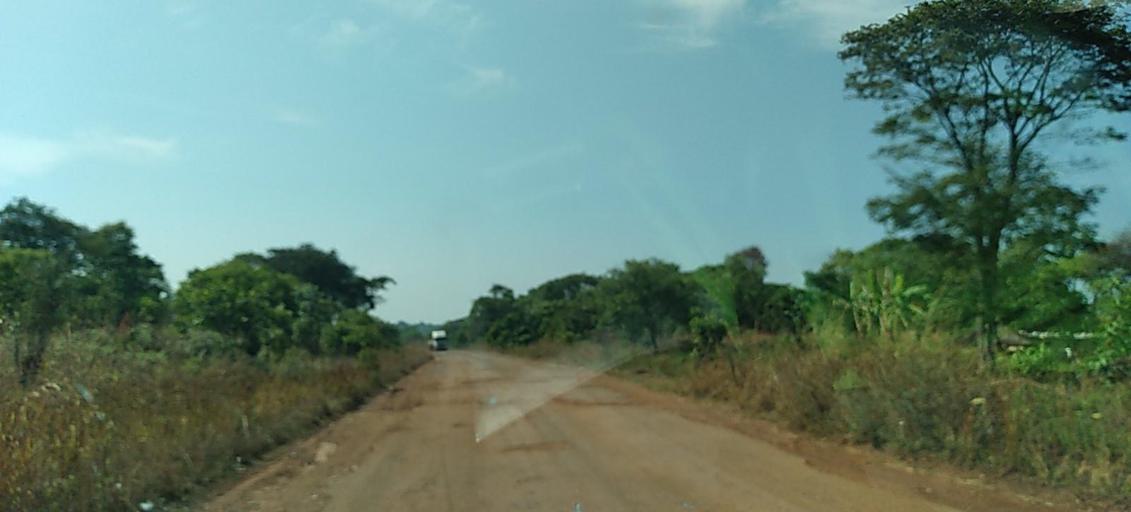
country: ZM
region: North-Western
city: Mwinilunga
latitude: -11.8009
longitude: 25.0759
